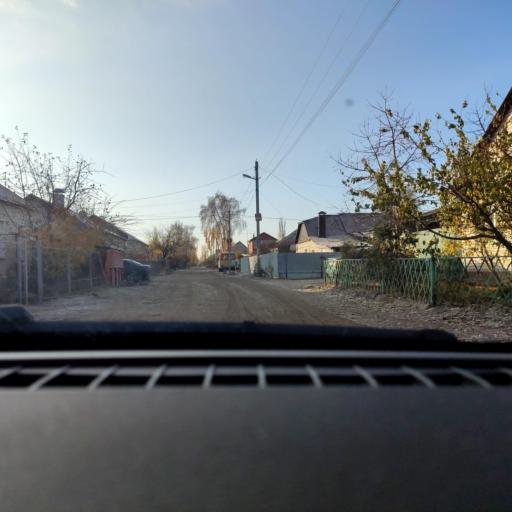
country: RU
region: Voronezj
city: Somovo
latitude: 51.7412
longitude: 39.2771
